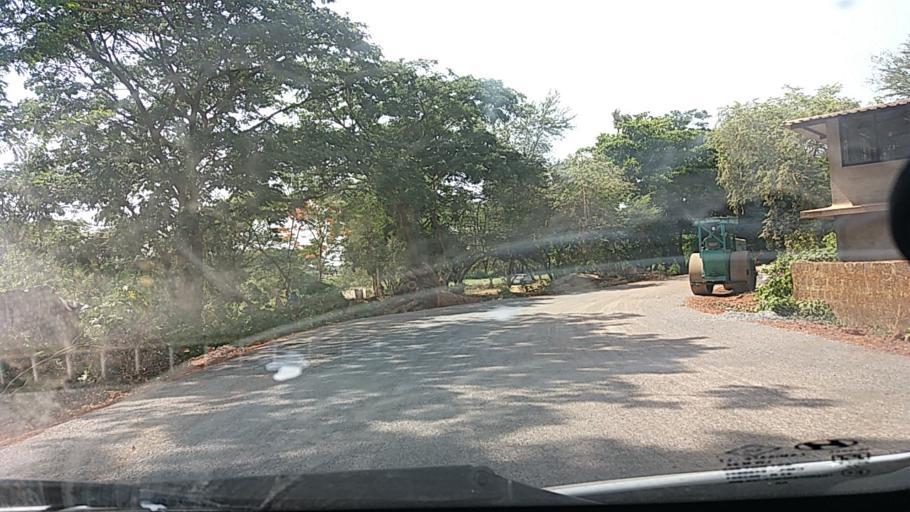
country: IN
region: Goa
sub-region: South Goa
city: Madgaon
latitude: 15.2753
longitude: 73.9525
